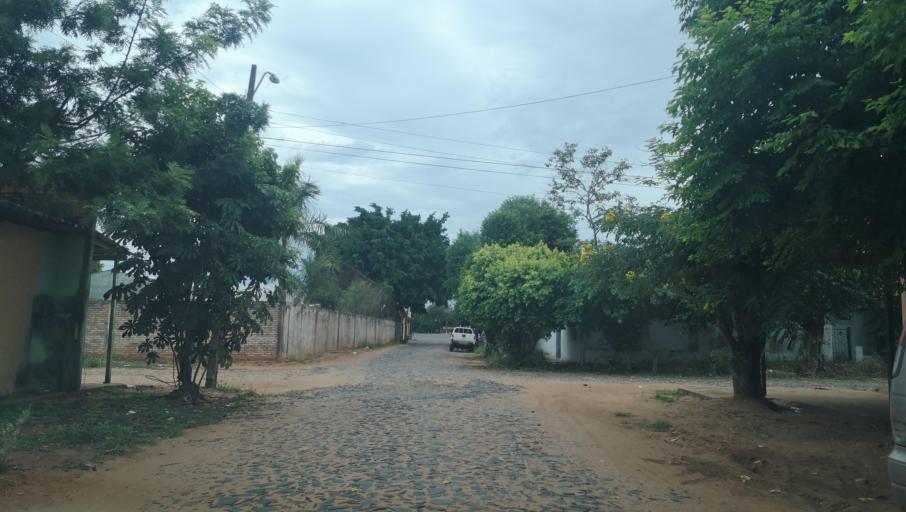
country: PY
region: San Pedro
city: Capiibary
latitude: -24.7300
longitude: -56.0180
